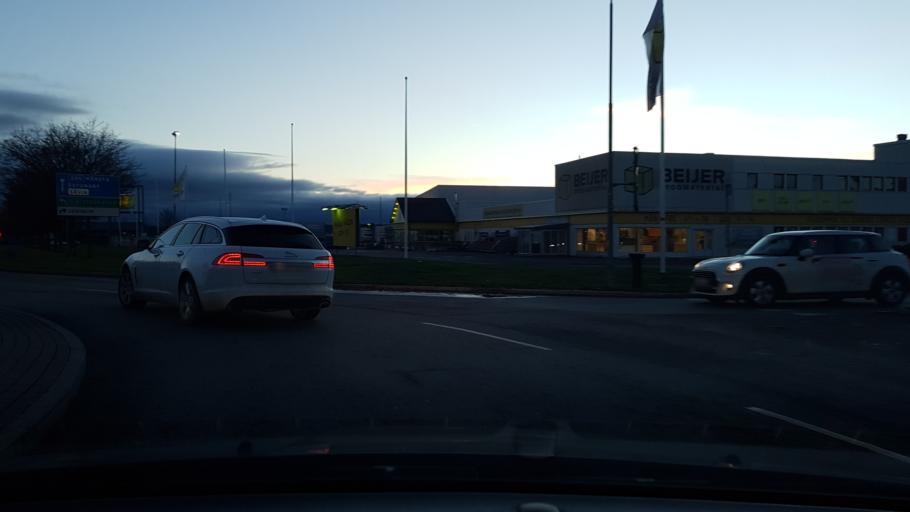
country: SE
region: Uppsala
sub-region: Uppsala Kommun
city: Saevja
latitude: 59.8456
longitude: 17.6900
